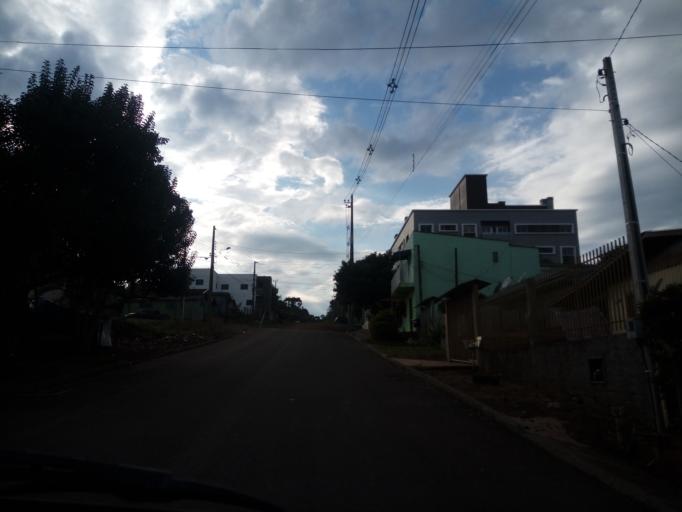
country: BR
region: Santa Catarina
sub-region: Chapeco
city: Chapeco
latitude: -27.0806
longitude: -52.6046
